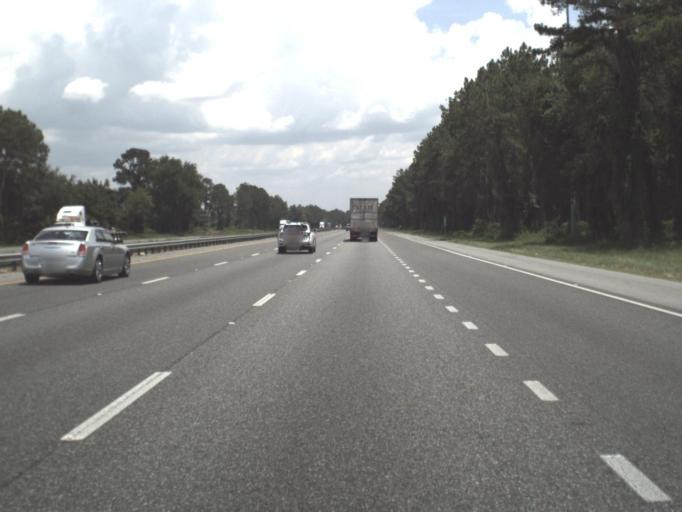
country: US
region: Florida
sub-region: Hamilton County
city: Jasper
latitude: 30.4462
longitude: -82.9291
